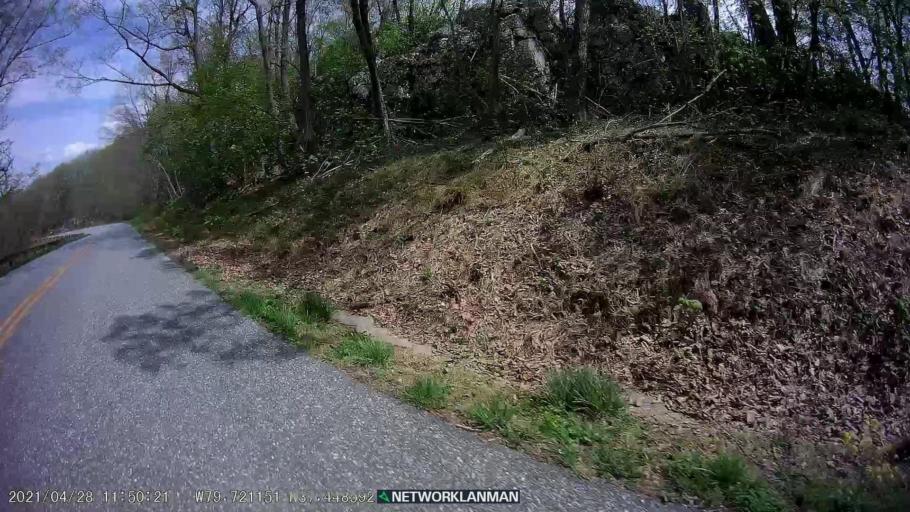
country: US
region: Virginia
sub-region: Botetourt County
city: Buchanan
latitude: 37.4489
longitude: -79.7208
